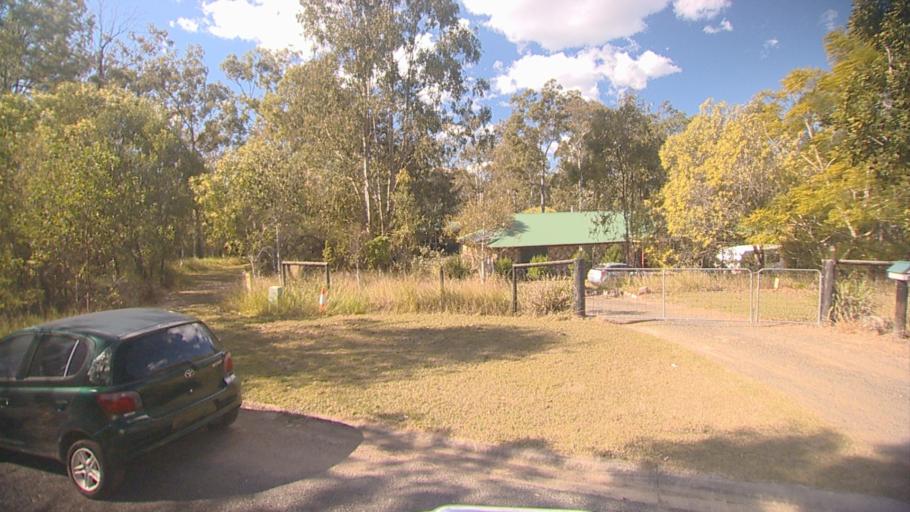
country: AU
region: Queensland
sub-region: Ipswich
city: Springfield Lakes
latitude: -27.7469
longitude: 152.9375
